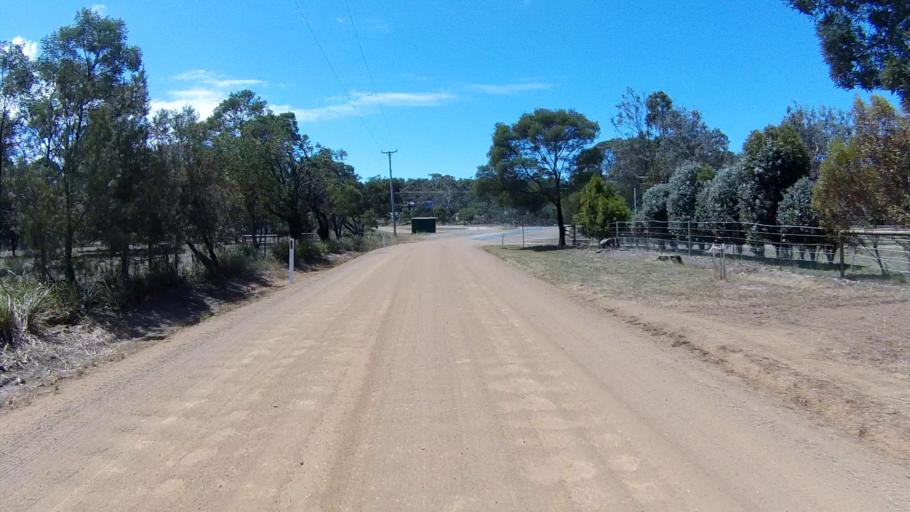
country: AU
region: Tasmania
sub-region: Clarence
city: Sandford
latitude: -42.9641
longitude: 147.4729
